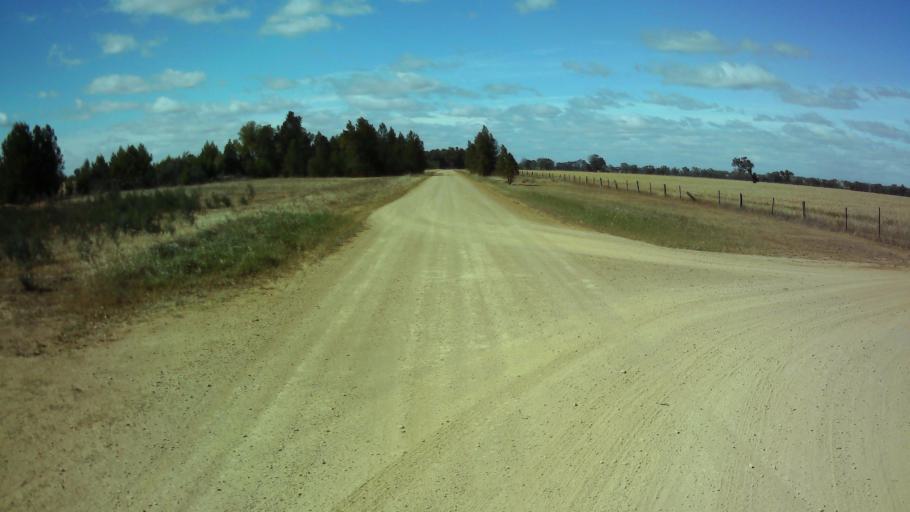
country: AU
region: New South Wales
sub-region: Weddin
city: Grenfell
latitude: -34.0305
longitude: 148.3174
